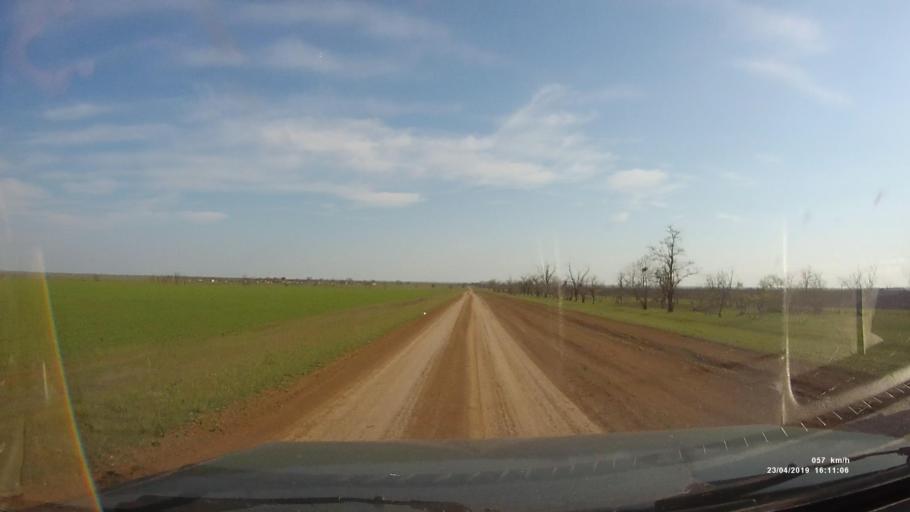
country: RU
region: Rostov
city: Remontnoye
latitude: 46.4769
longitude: 43.1231
